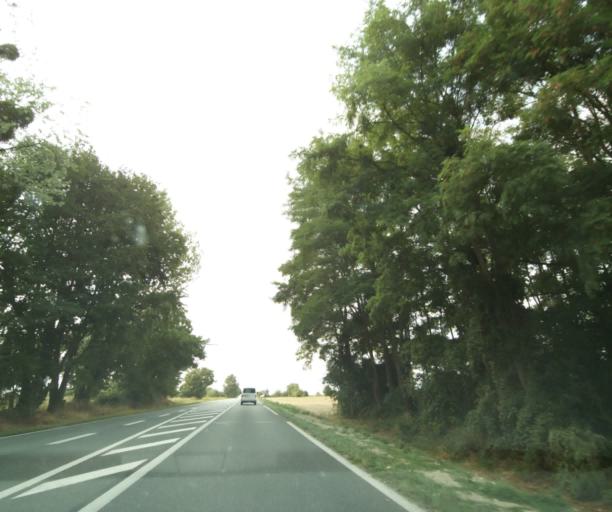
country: FR
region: Centre
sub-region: Departement de l'Indre
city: Clion
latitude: 46.9333
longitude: 1.2607
